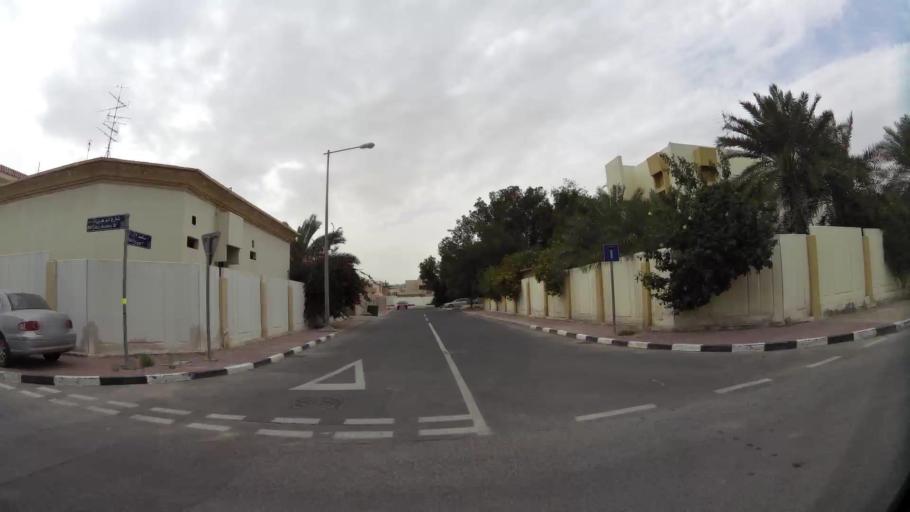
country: QA
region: Baladiyat ad Dawhah
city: Doha
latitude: 25.3331
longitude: 51.5053
